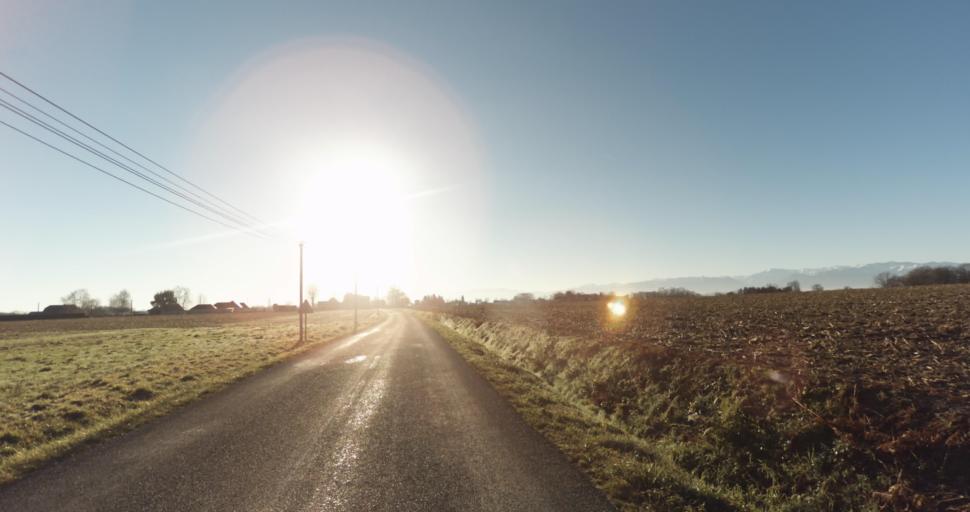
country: FR
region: Aquitaine
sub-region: Departement des Pyrenees-Atlantiques
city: Ousse
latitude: 43.3141
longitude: -0.2370
